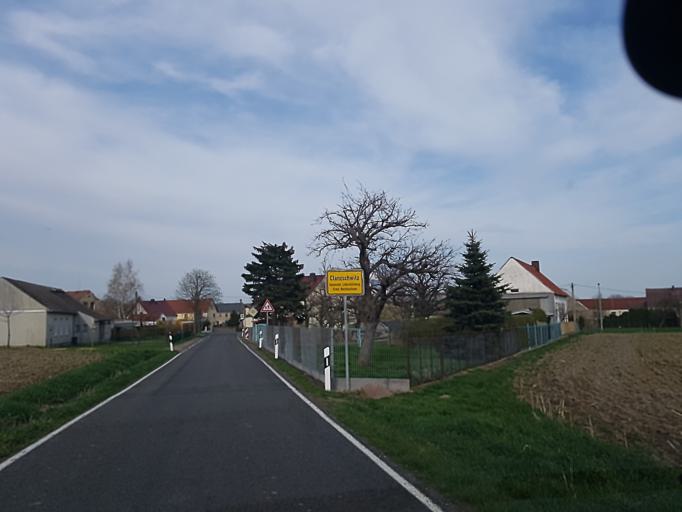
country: DE
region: Saxony
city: Cavertitz
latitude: 51.3432
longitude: 13.1531
